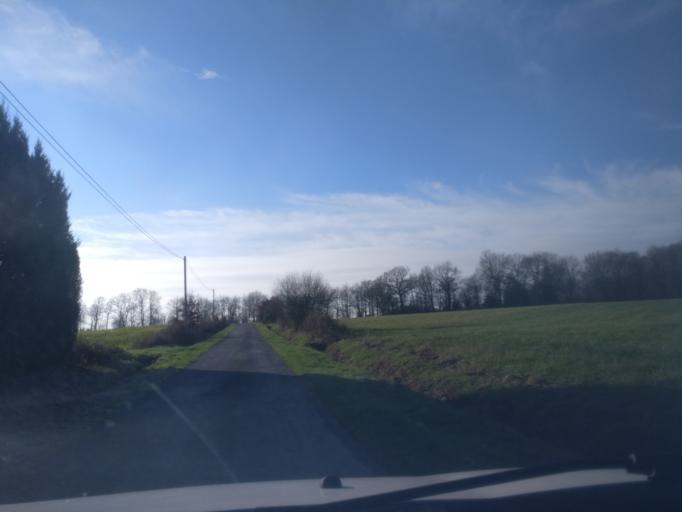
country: FR
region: Brittany
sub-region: Departement d'Ille-et-Vilaine
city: Livre-sur-Changeon
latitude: 48.2352
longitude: -1.3511
